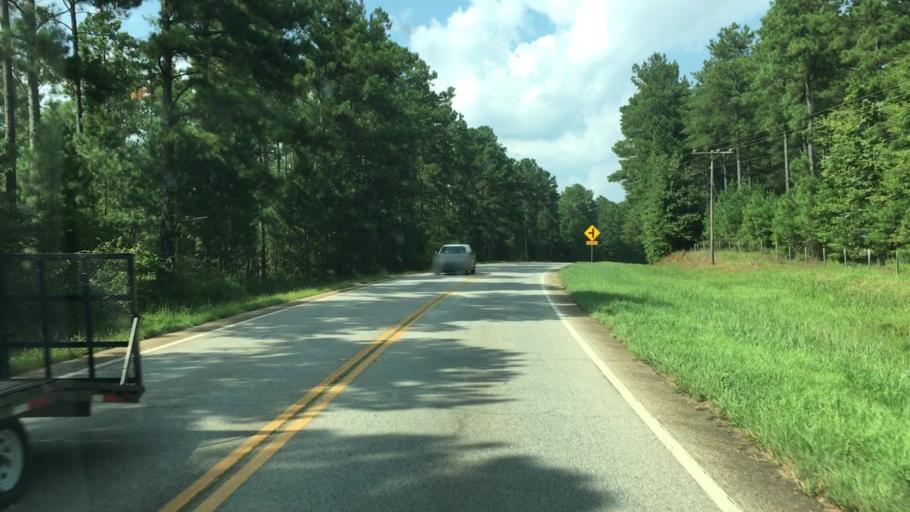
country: US
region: Georgia
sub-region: Monroe County
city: Forsyth
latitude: 33.1290
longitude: -83.8718
